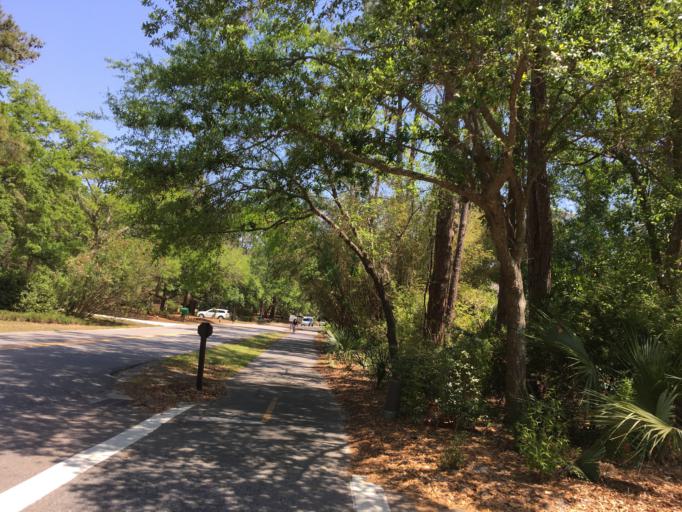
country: US
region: Georgia
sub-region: Chatham County
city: Tybee Island
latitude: 32.1109
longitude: -80.8206
